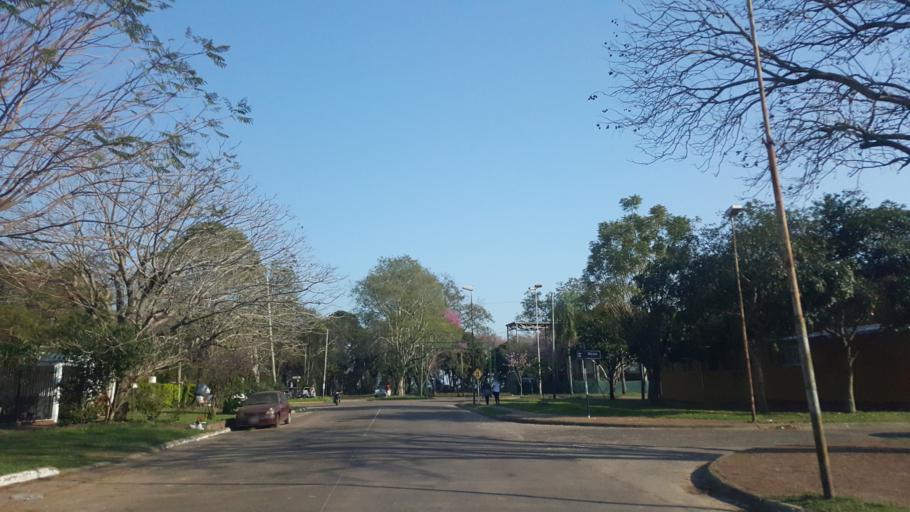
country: AR
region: Corrientes
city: Ituzaingo
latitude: -27.5808
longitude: -56.6821
